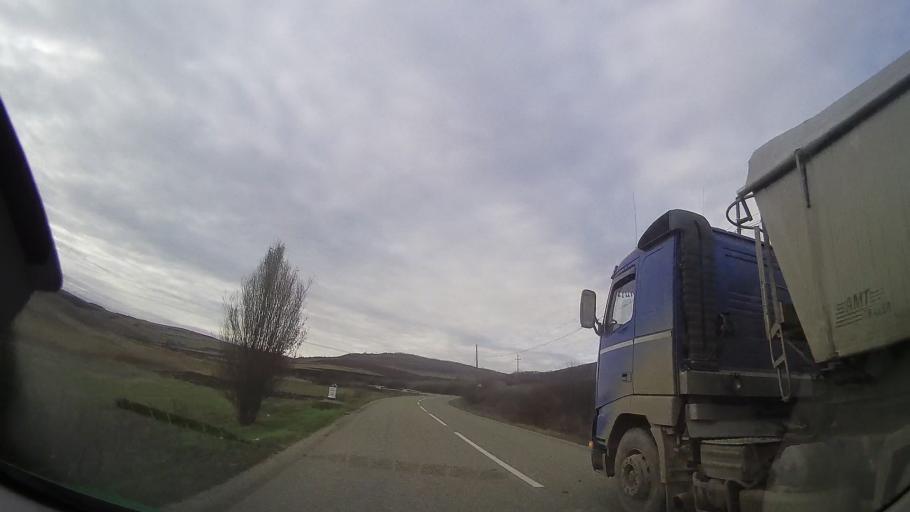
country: RO
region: Bistrita-Nasaud
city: Frunzi
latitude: 46.8966
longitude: 24.3122
